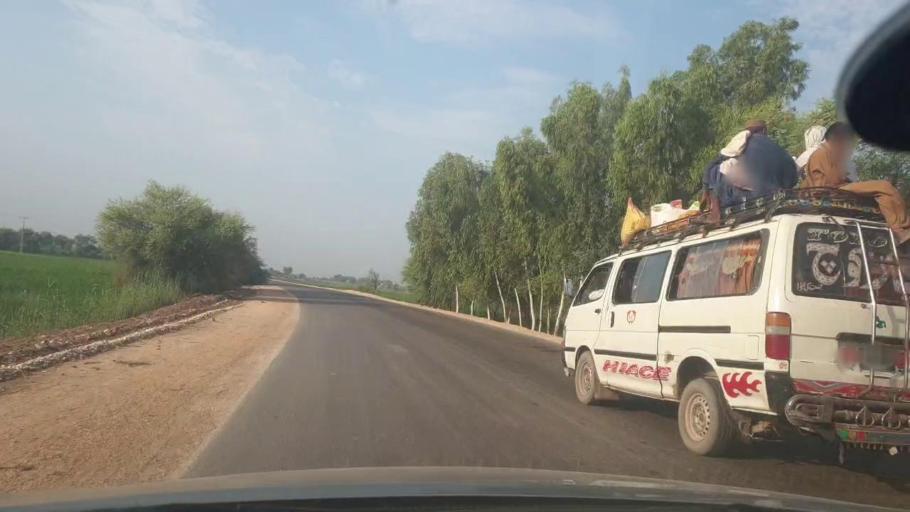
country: PK
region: Sindh
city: Jacobabad
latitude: 28.2410
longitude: 68.3927
